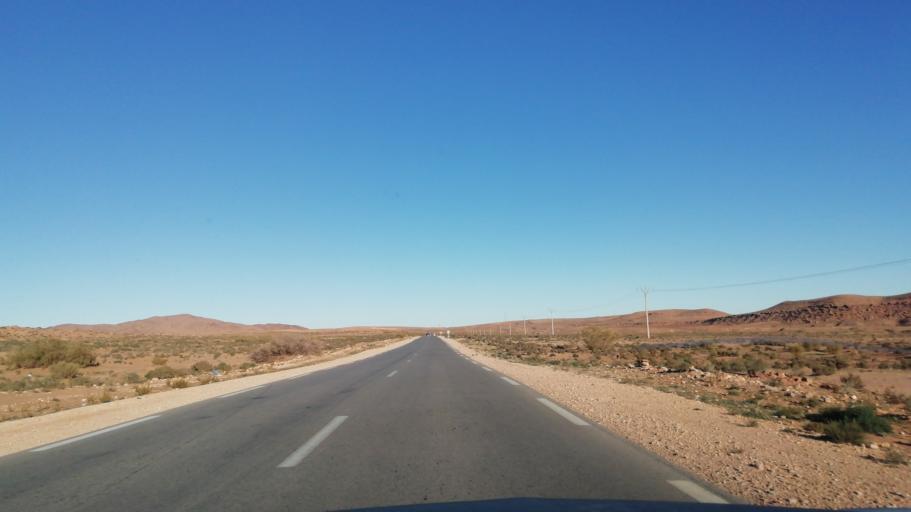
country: DZ
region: El Bayadh
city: El Abiodh Sidi Cheikh
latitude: 33.1641
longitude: 0.4102
